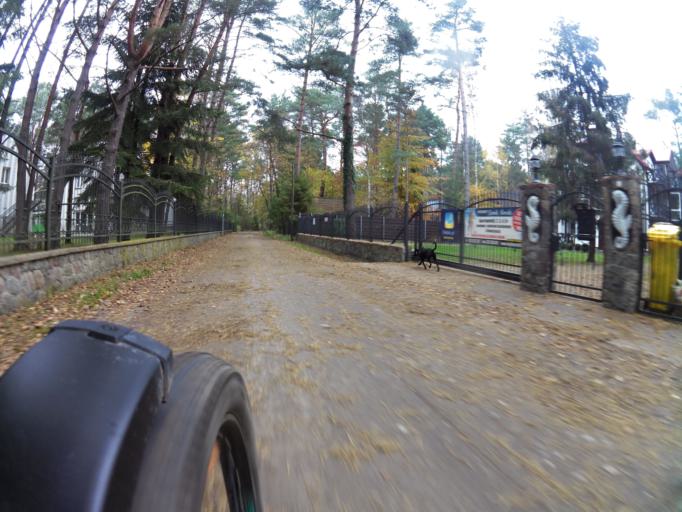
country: PL
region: Pomeranian Voivodeship
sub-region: Powiat pucki
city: Wierzchucino
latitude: 54.8284
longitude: 18.0815
